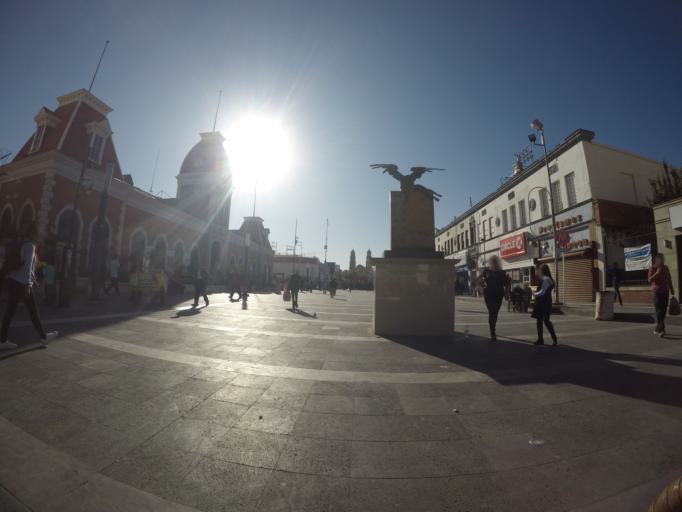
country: MX
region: Chihuahua
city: Ciudad Juarez
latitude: 31.7389
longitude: -106.4837
